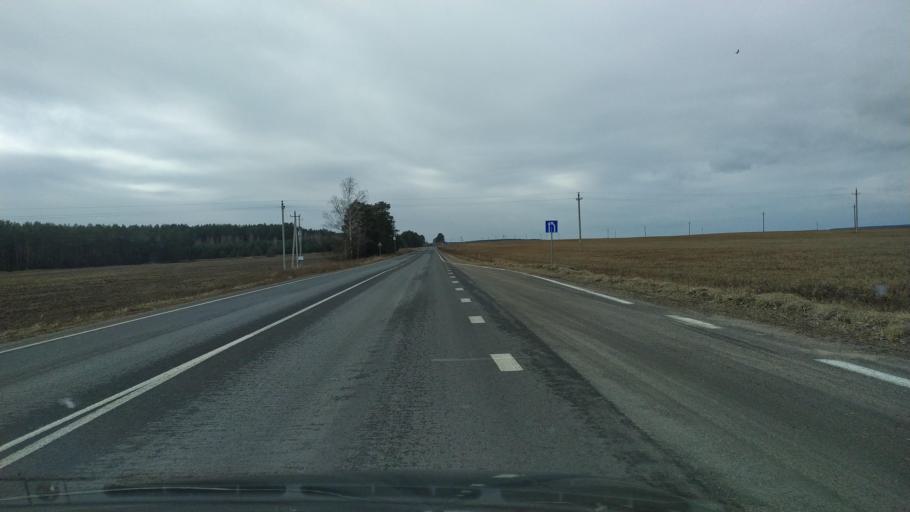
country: BY
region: Brest
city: Kamyanyets
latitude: 52.3998
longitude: 23.8844
